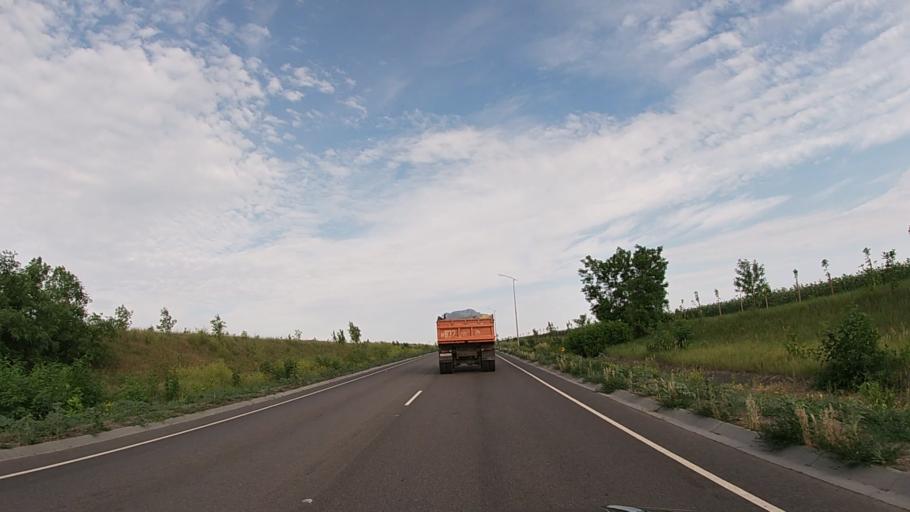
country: RU
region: Belgorod
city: Severnyy
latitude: 50.6705
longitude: 36.4846
